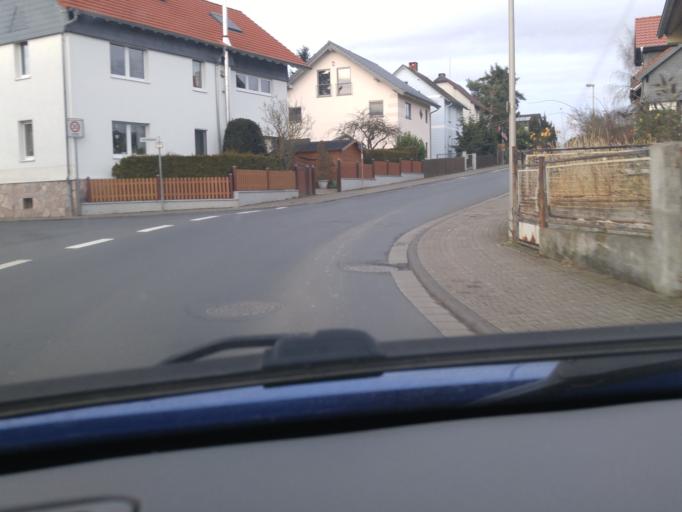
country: DE
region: Hesse
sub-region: Regierungsbezirk Darmstadt
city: Wehrheim
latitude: 50.3049
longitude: 8.5734
